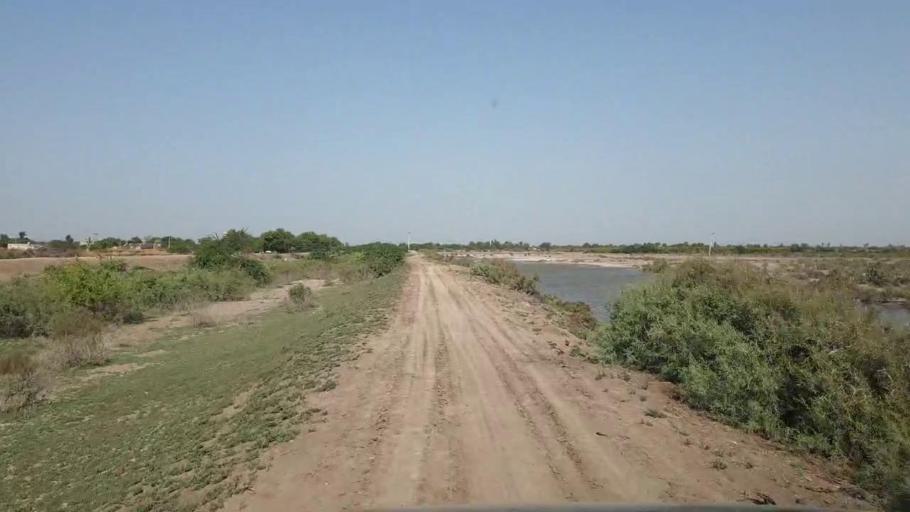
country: PK
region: Sindh
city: Tando Bago
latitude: 24.6606
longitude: 69.0686
